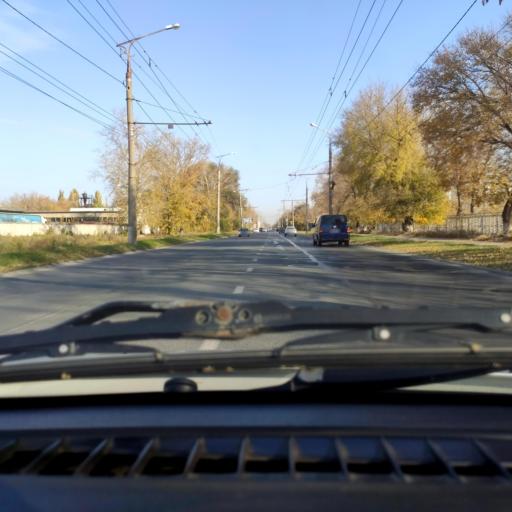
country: RU
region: Samara
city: Tol'yatti
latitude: 53.5266
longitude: 49.4357
